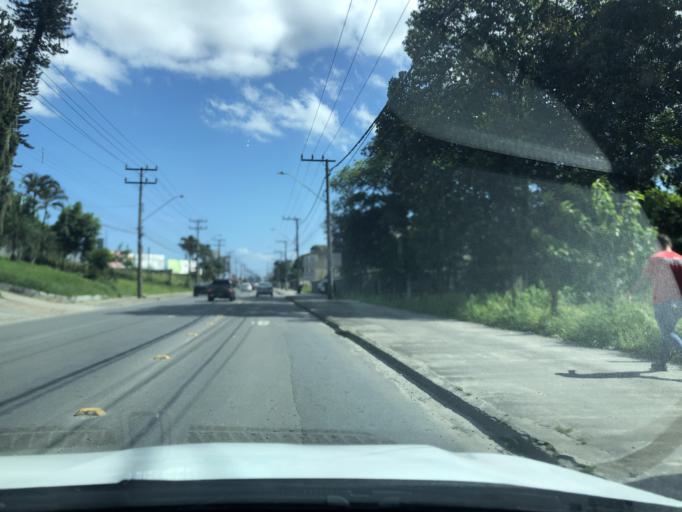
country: BR
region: Santa Catarina
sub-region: Joinville
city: Joinville
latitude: -26.2605
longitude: -48.8516
